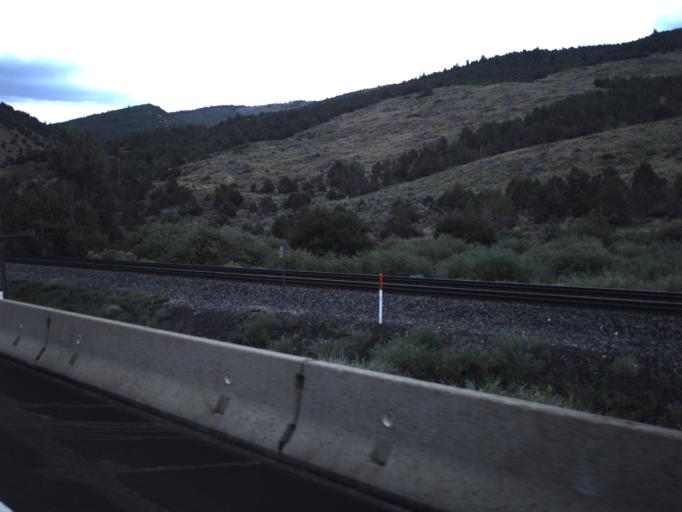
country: US
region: Utah
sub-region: Utah County
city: Mapleton
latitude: 39.9534
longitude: -111.2932
